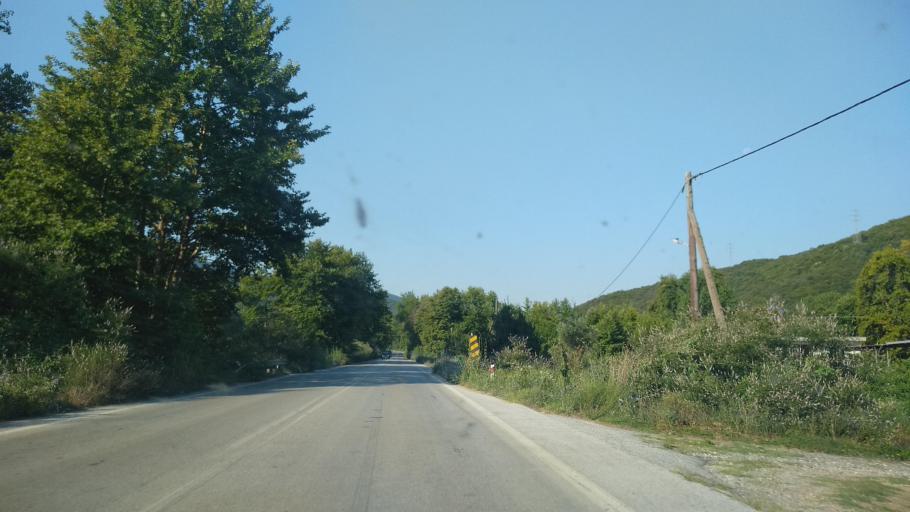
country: GR
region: Central Macedonia
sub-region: Nomos Thessalonikis
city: Stavros
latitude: 40.6843
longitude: 23.6769
